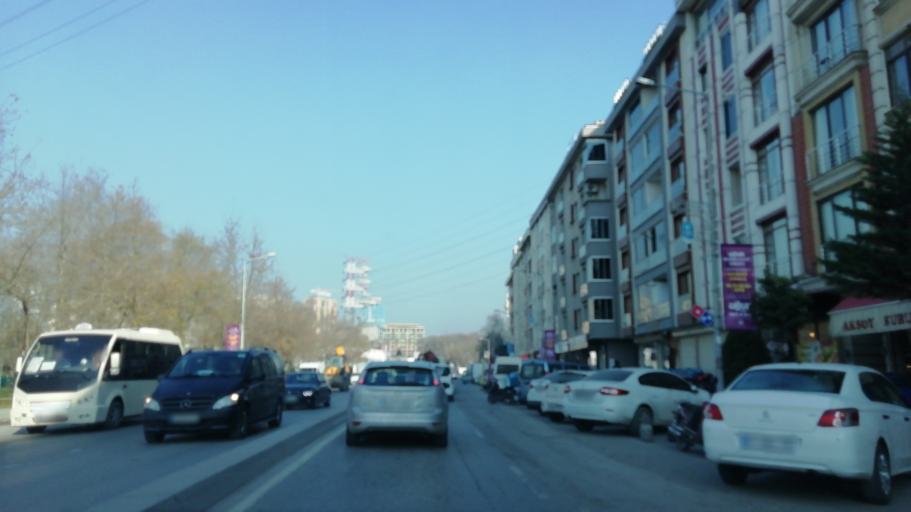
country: TR
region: Istanbul
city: Sisli
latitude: 41.0805
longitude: 28.9515
